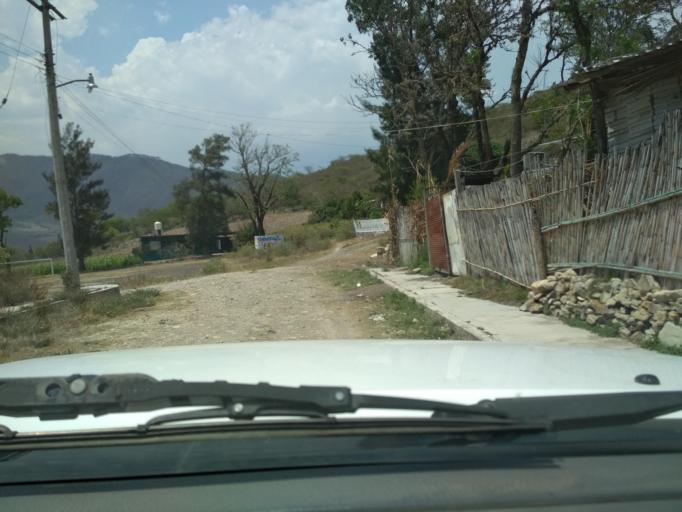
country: MX
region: Veracruz
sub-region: Acultzingo
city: Acatla
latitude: 18.7515
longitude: -97.2186
